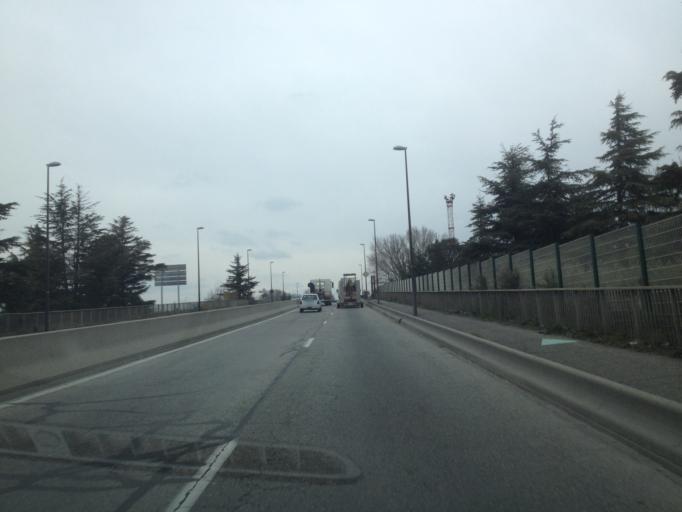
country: FR
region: Provence-Alpes-Cote d'Azur
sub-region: Departement du Vaucluse
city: Avignon
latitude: 43.9364
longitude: 4.8322
